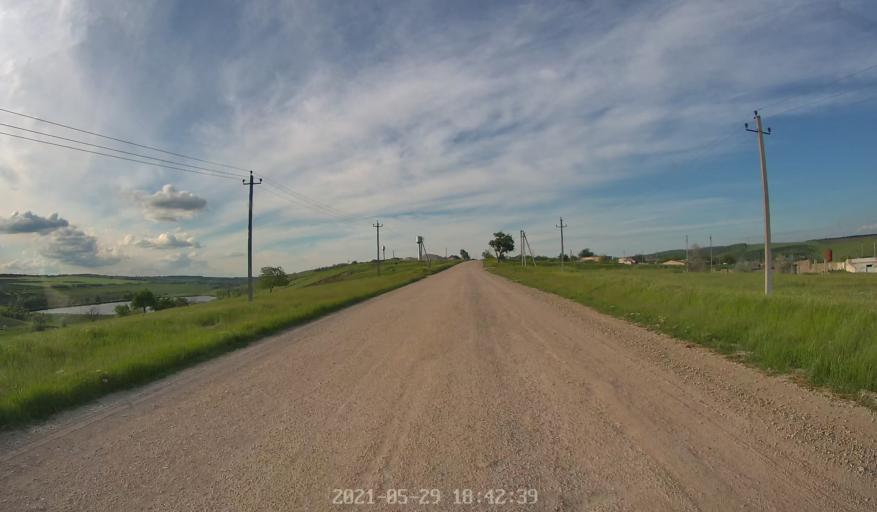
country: MD
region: Chisinau
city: Singera
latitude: 46.8136
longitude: 28.9626
